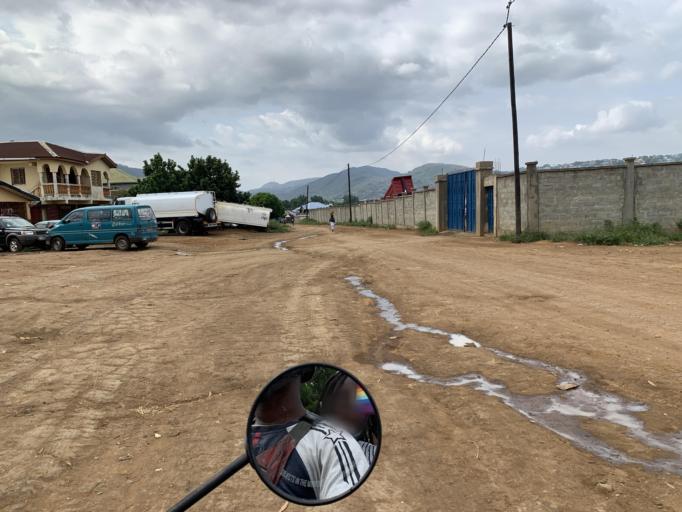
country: SL
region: Western Area
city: Hastings
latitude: 8.3898
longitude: -13.1482
